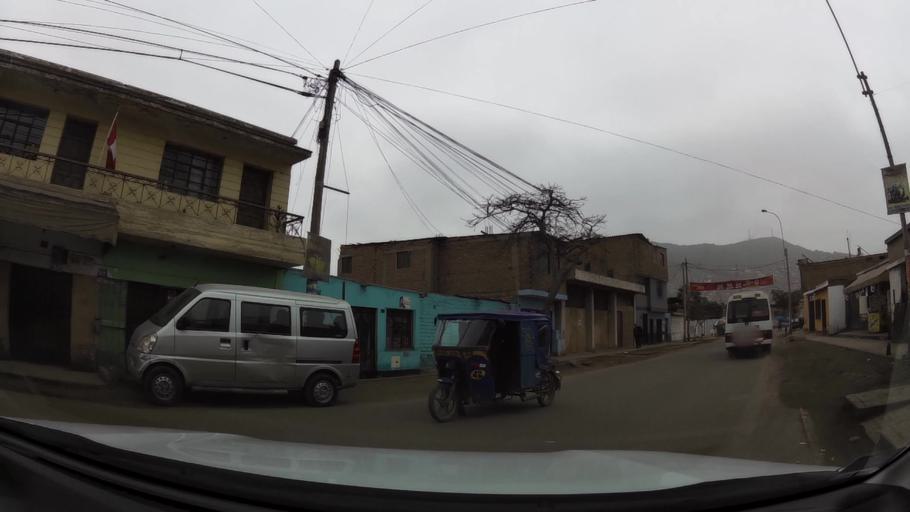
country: PE
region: Lima
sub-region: Lima
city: Cieneguilla
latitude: -12.2101
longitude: -76.9067
